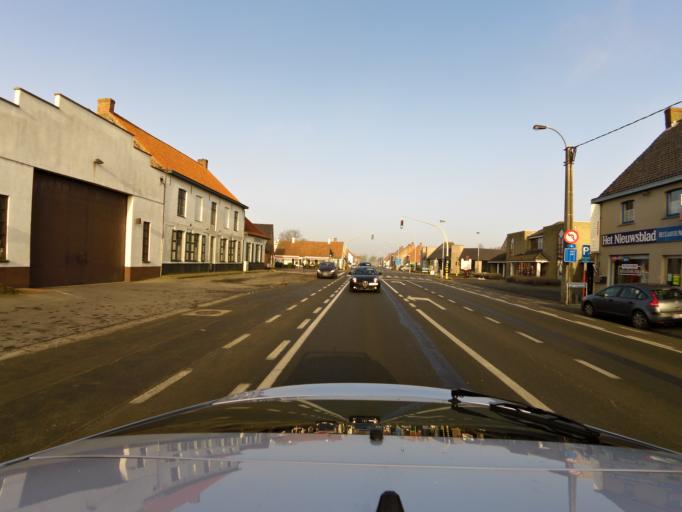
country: BE
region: Flanders
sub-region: Provincie West-Vlaanderen
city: Ichtegem
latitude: 51.1012
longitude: 3.0323
